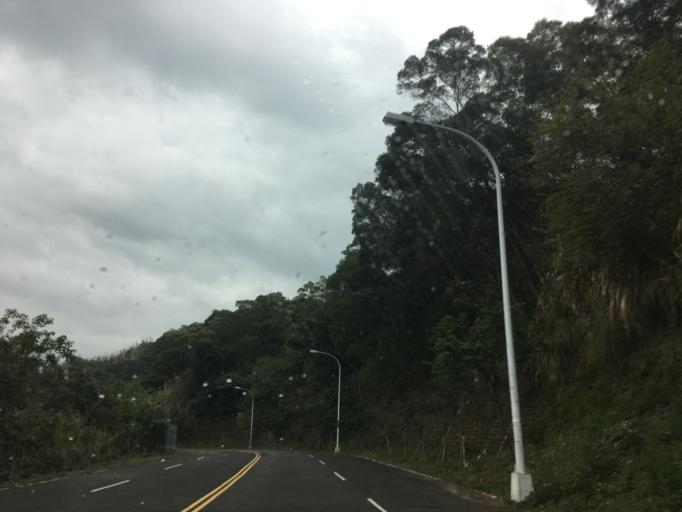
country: TW
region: Taiwan
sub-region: Taichung City
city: Taichung
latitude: 24.0637
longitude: 120.7222
